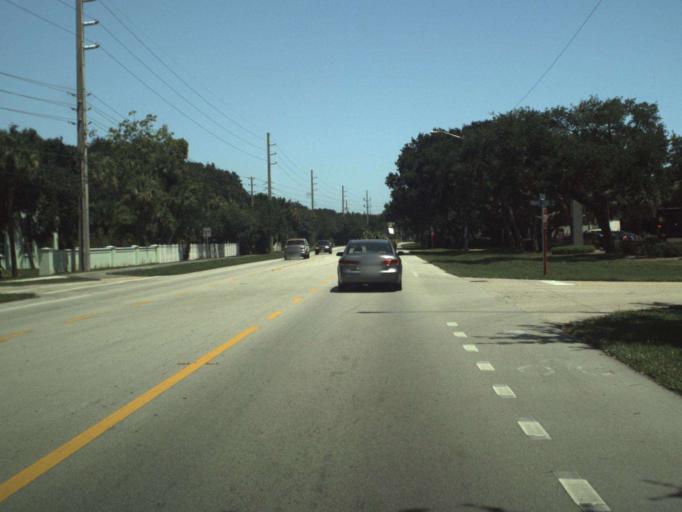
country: US
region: Florida
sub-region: Indian River County
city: South Beach
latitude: 27.6283
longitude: -80.3550
